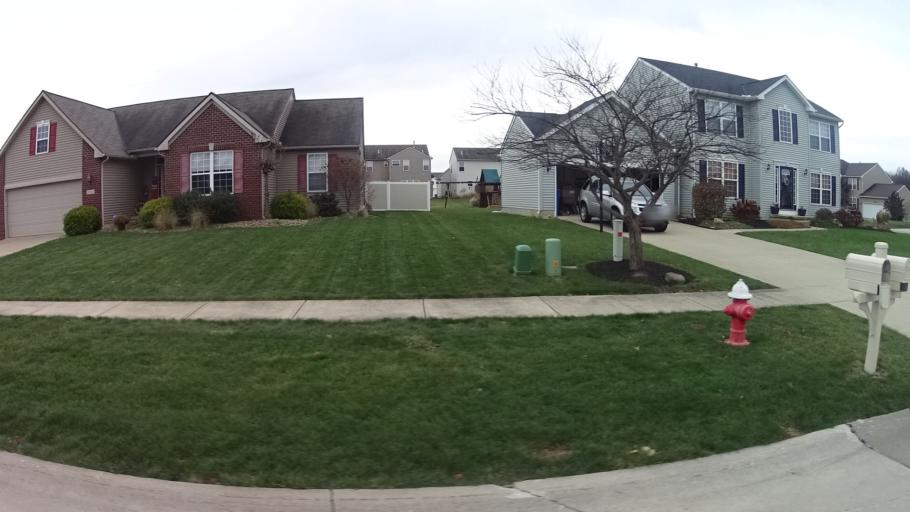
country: US
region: Ohio
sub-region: Lorain County
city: Avon
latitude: 41.4162
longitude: -82.0535
